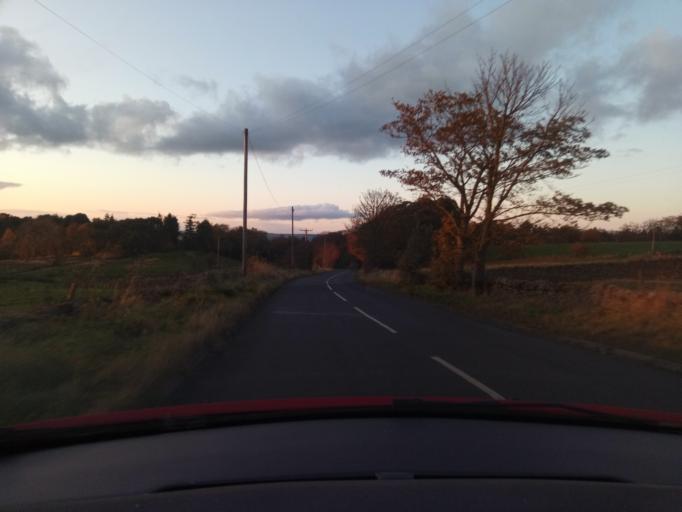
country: GB
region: England
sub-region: Northumberland
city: Bardon Mill
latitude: 54.9423
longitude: -2.2668
